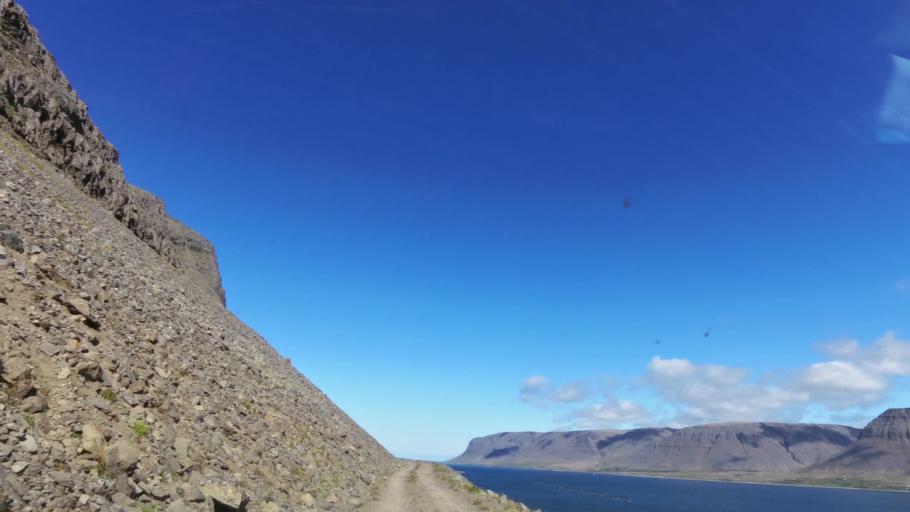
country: IS
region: West
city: Olafsvik
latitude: 65.6273
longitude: -23.9026
